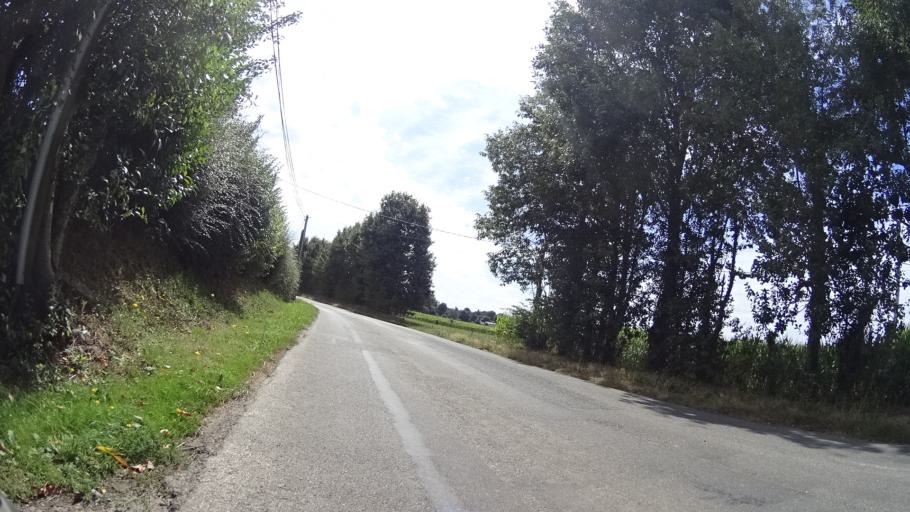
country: FR
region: Brittany
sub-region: Departement d'Ille-et-Vilaine
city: La Meziere
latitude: 48.2272
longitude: -1.7432
